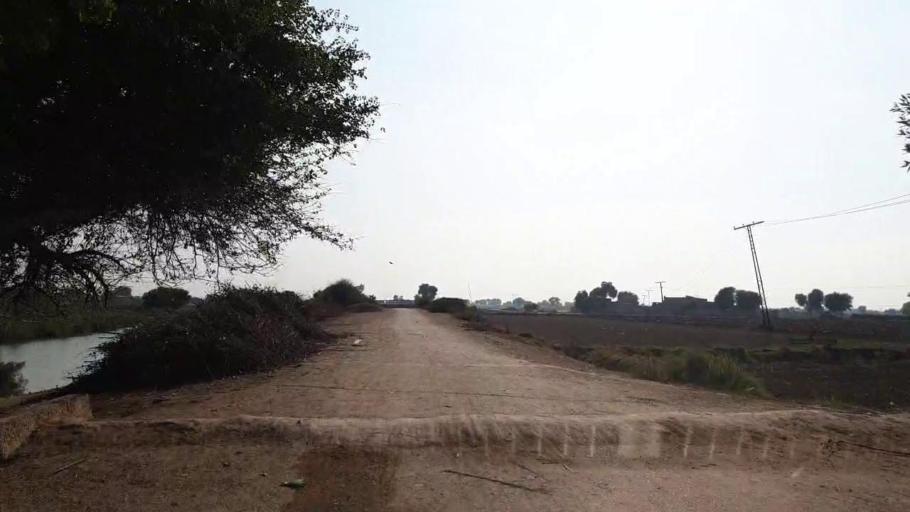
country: PK
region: Sindh
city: Sehwan
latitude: 26.4442
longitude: 67.8099
